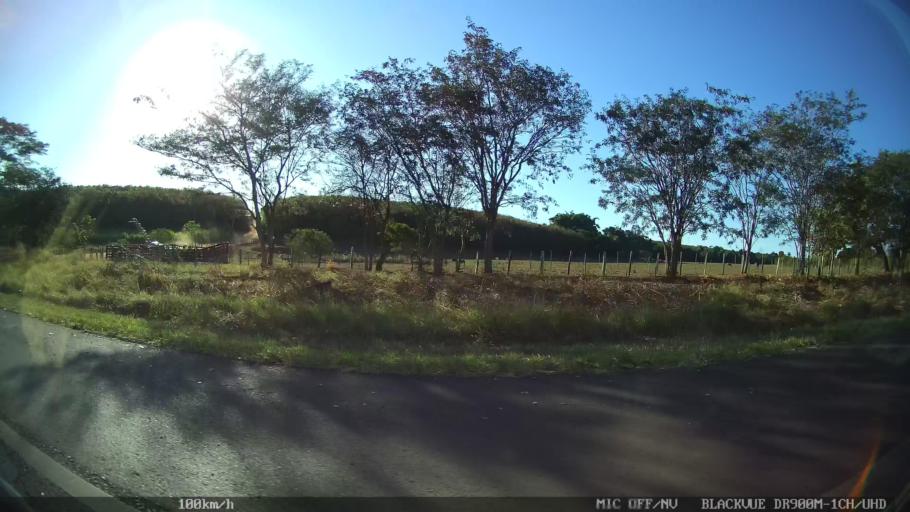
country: BR
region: Sao Paulo
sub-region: Guapiacu
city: Guapiacu
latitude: -20.7687
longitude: -49.2083
